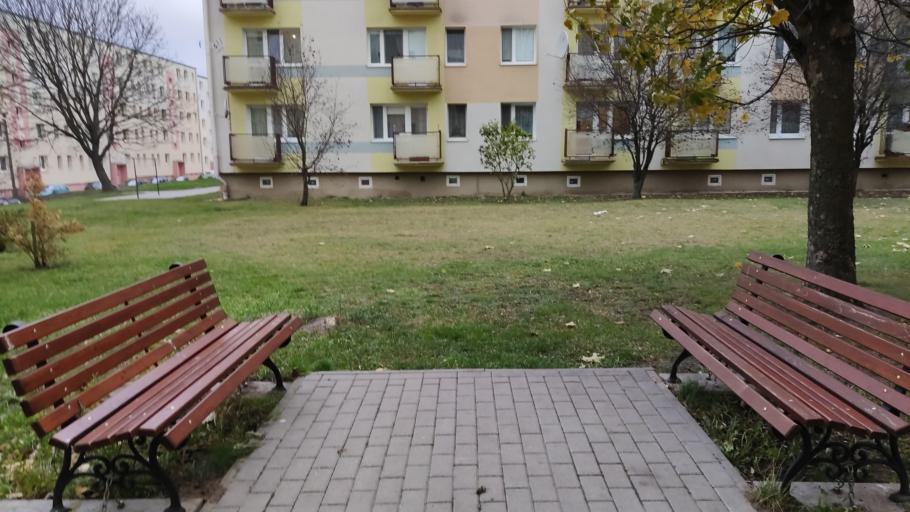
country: PL
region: Kujawsko-Pomorskie
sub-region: Powiat zninski
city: Barcin
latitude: 52.8516
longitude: 17.9494
